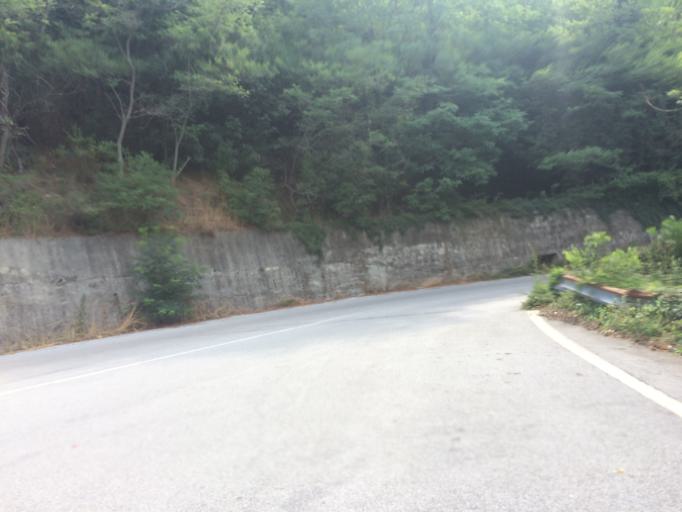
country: IT
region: Liguria
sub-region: Provincia di Savona
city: San Giovanni
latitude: 44.4042
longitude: 8.4898
